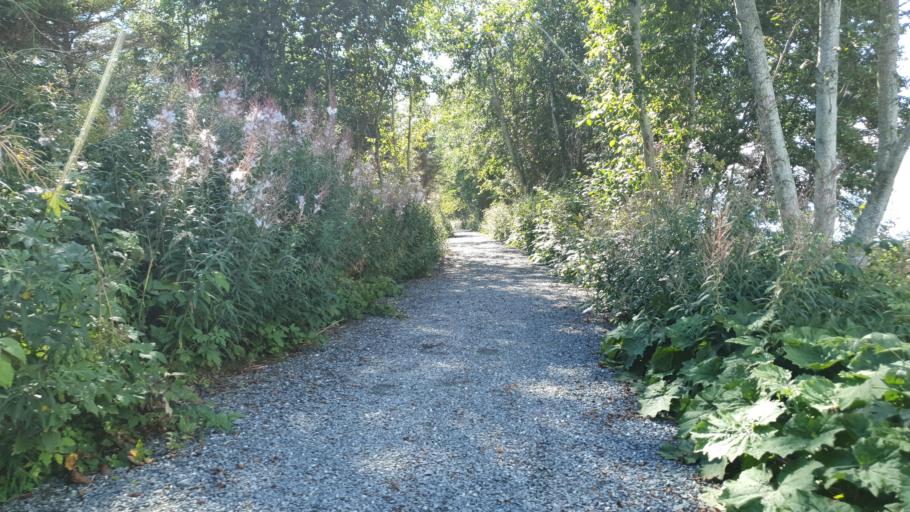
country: NO
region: Nord-Trondelag
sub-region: Levanger
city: Levanger
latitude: 63.7783
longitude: 11.3826
